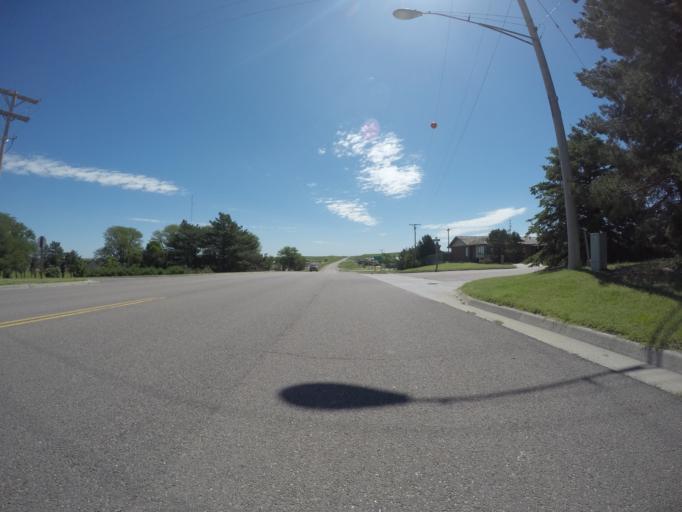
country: US
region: Kansas
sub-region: Rawlins County
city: Atwood
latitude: 39.8133
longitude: -101.0376
